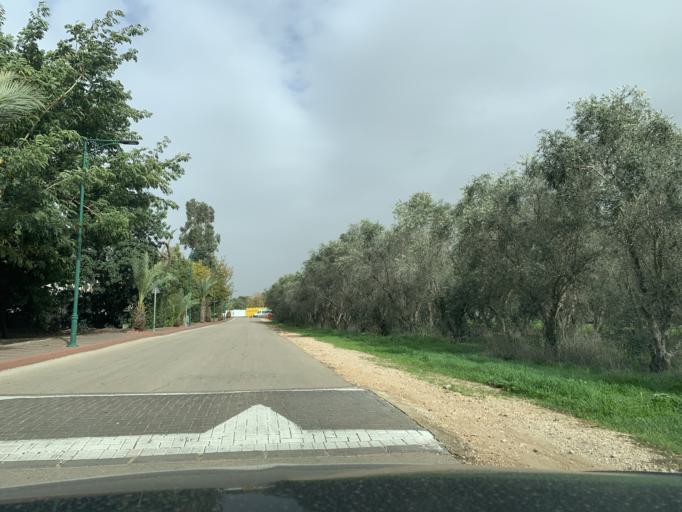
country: IL
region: Central District
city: Jaljulya
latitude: 32.1565
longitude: 34.9434
